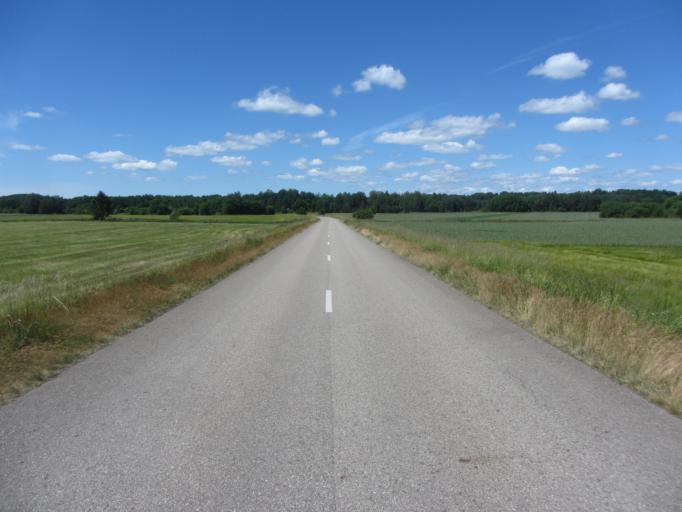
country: LT
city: Jieznas
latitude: 54.7482
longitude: 24.1446
